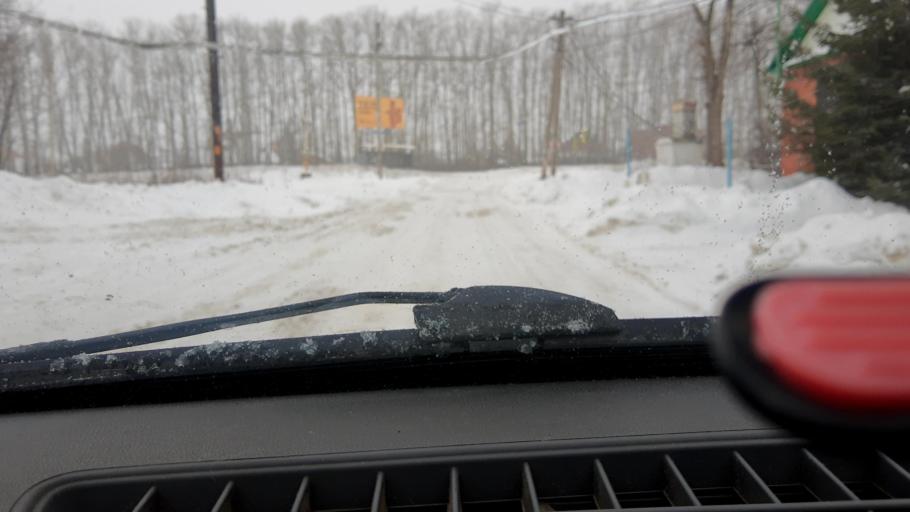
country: RU
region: Bashkortostan
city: Kabakovo
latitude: 54.6291
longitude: 56.1015
